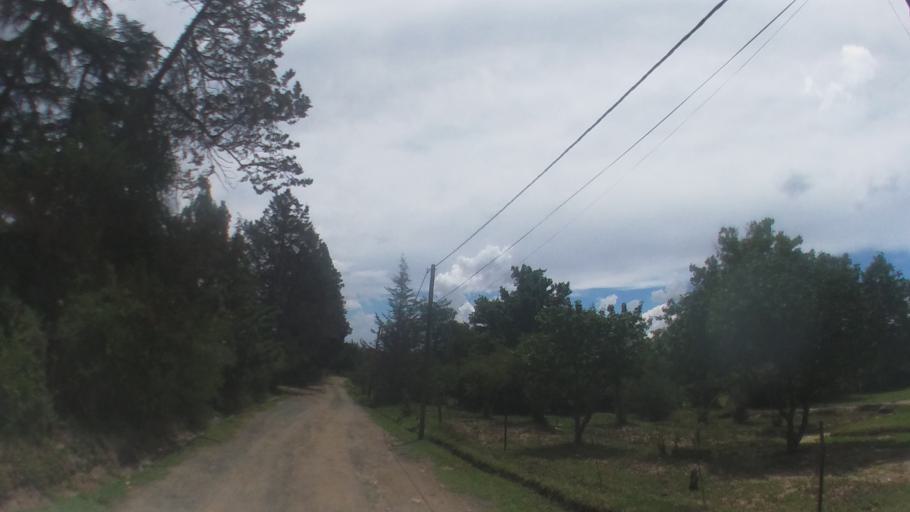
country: LS
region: Maseru
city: Nako
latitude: -29.6232
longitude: 27.5078
